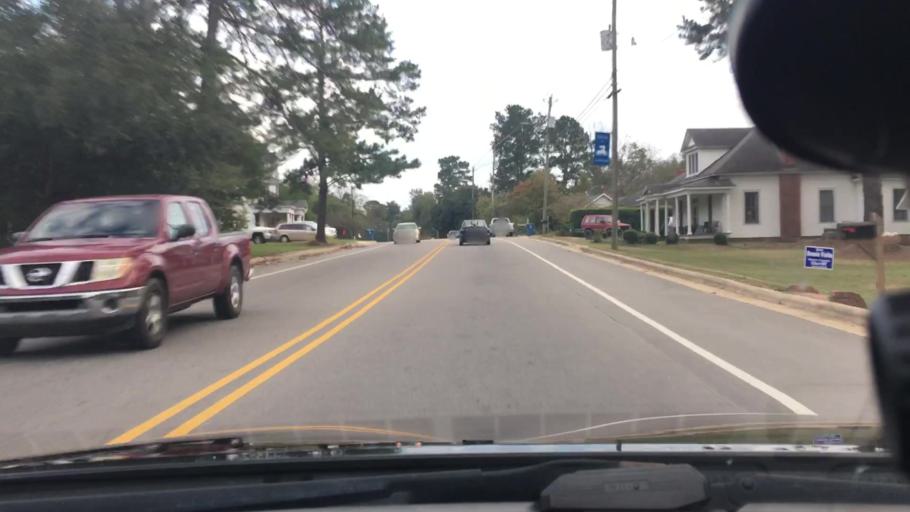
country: US
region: North Carolina
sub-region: Moore County
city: Carthage
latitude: 35.3526
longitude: -79.4227
